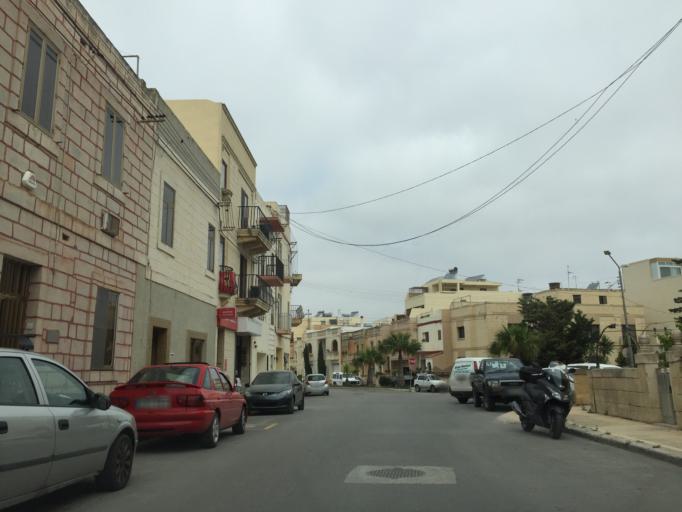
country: MT
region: Ir-Rabat
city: Rabat
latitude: 35.8835
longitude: 14.3900
